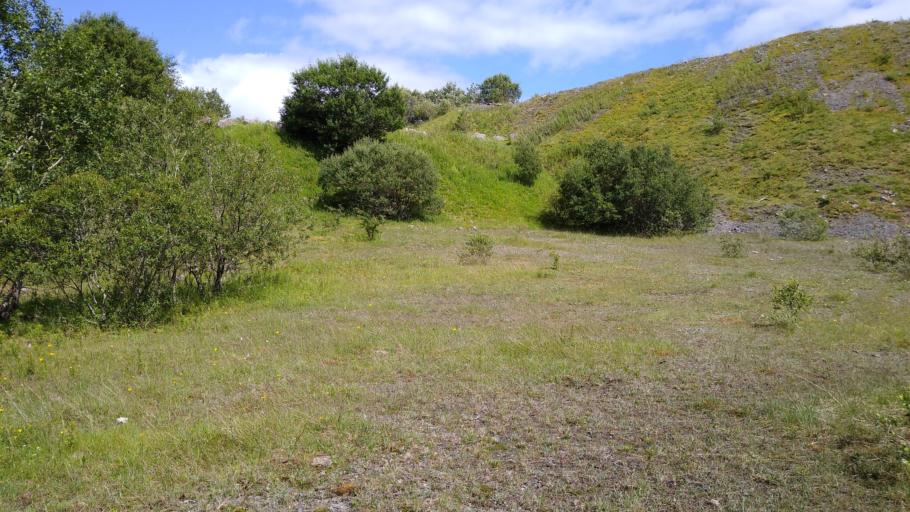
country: GB
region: England
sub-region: Cumbria
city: Aspatria
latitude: 54.7166
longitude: -3.3085
